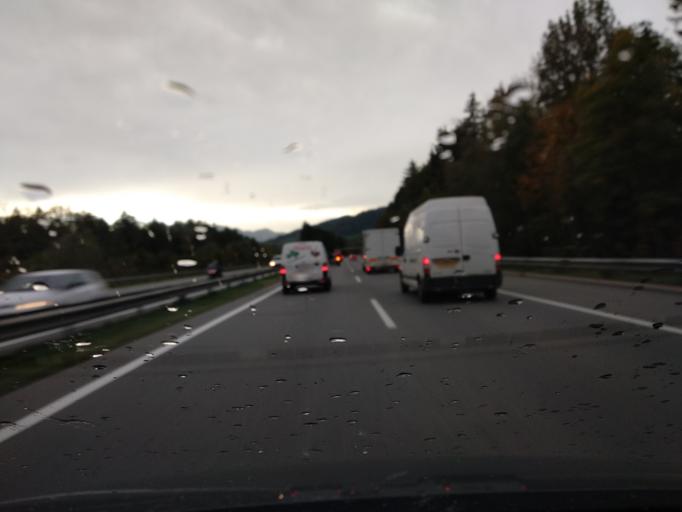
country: AT
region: Vorarlberg
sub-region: Politischer Bezirk Feldkirch
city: Satteins
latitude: 47.2124
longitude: 9.6625
